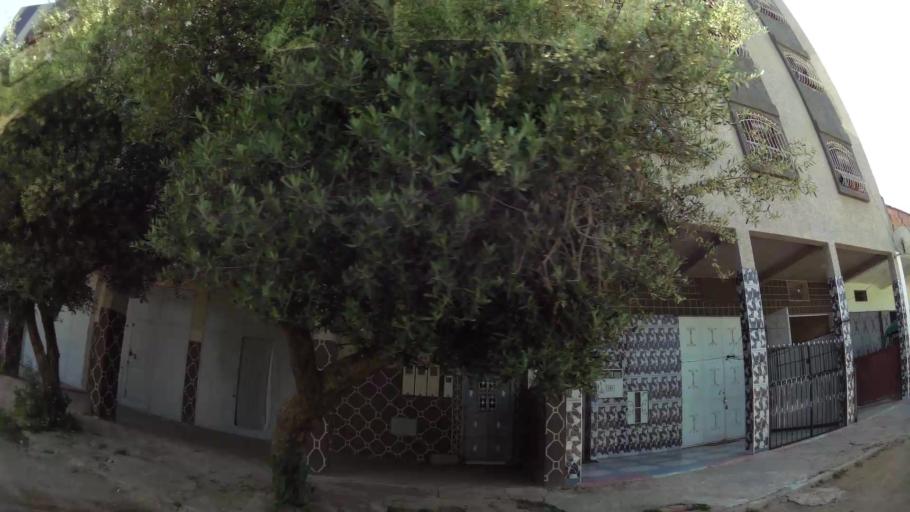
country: MA
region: Rabat-Sale-Zemmour-Zaer
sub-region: Khemisset
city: Khemisset
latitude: 33.8102
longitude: -6.0731
